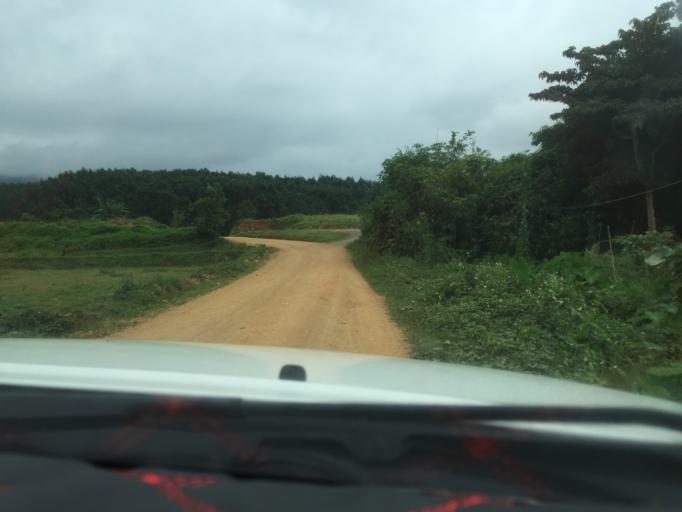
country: TH
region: Phayao
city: Phu Sang
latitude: 19.6939
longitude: 100.5012
